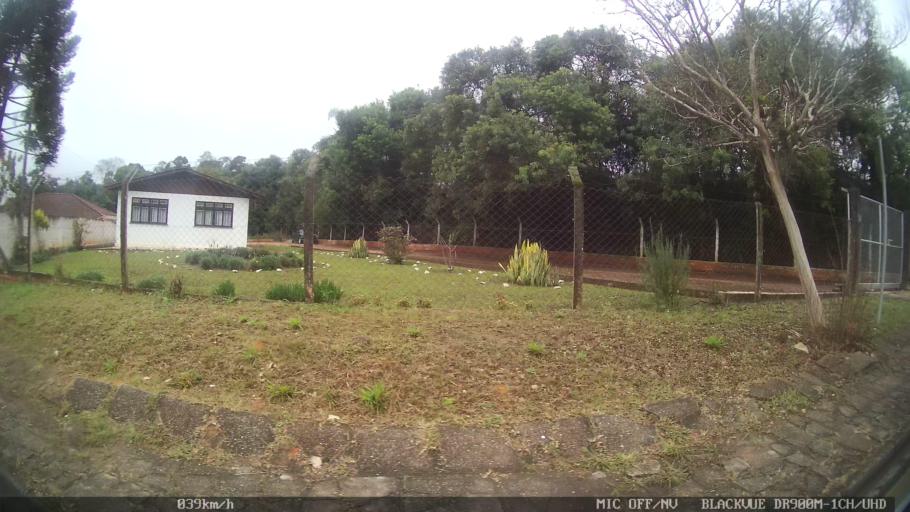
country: BR
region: Parana
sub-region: Sao Jose Dos Pinhais
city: Sao Jose dos Pinhais
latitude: -25.5853
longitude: -49.1715
